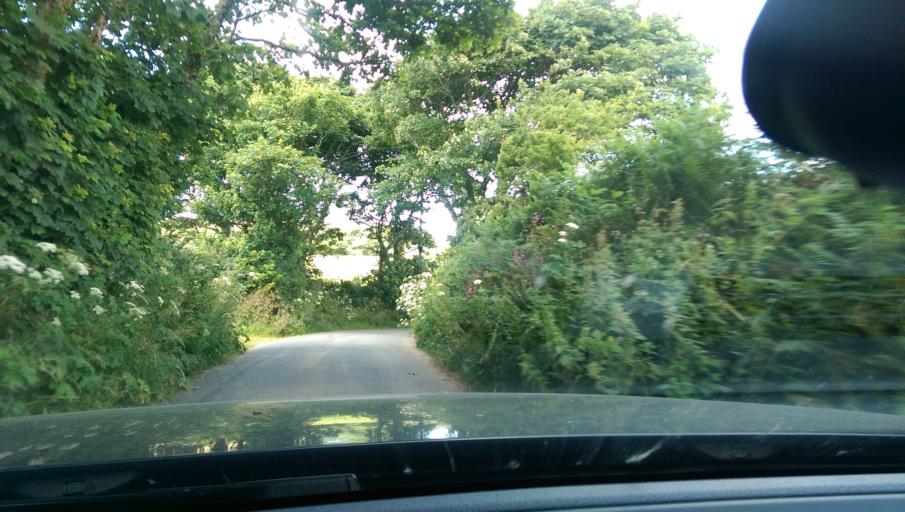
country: GB
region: England
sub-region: Cornwall
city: St. Buryan
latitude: 50.0961
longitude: -5.6155
